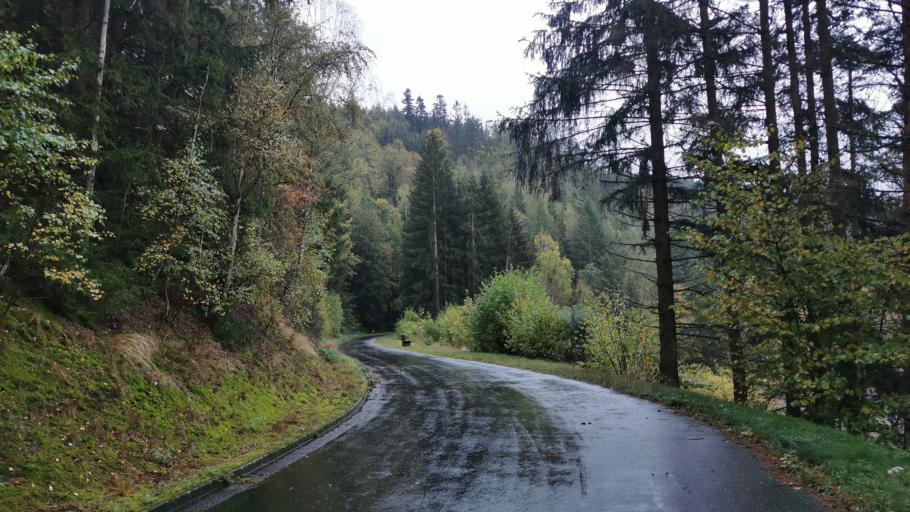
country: DE
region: Bavaria
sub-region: Upper Franconia
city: Nordhalben
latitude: 50.3384
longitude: 11.4906
